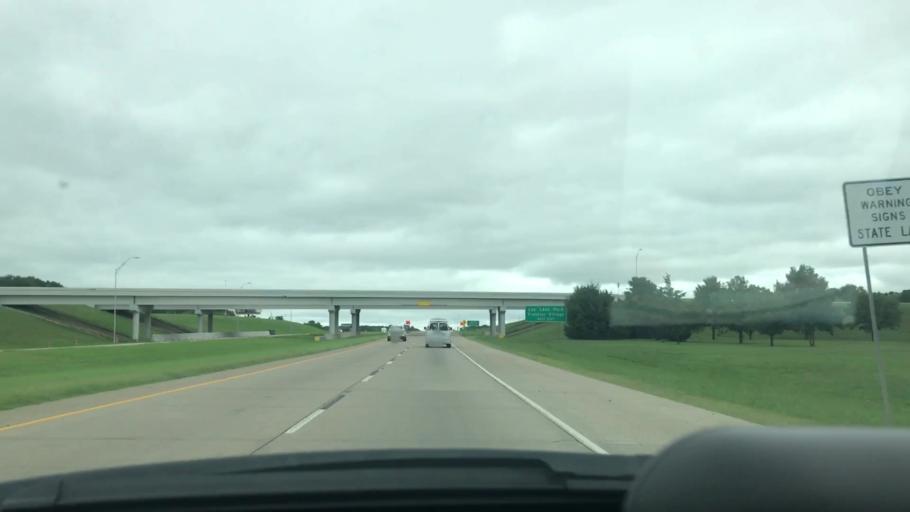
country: US
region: Texas
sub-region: Grayson County
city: Denison
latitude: 33.7194
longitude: -96.5852
